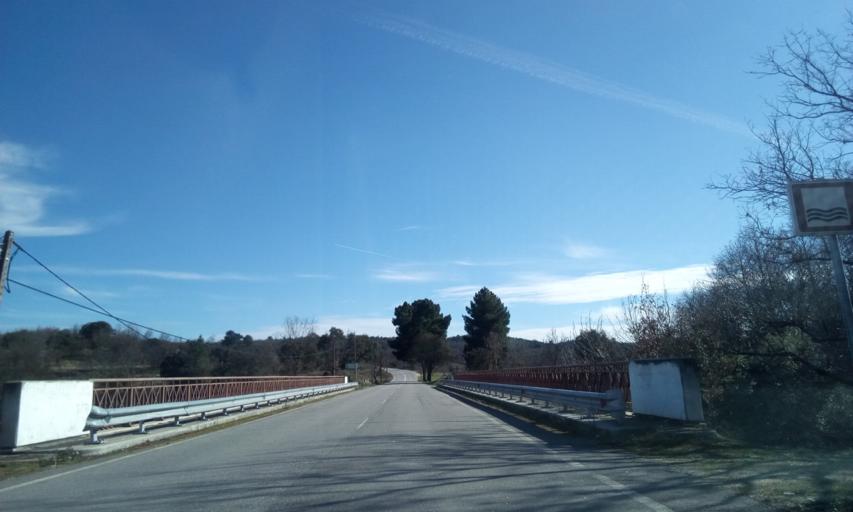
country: PT
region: Guarda
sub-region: Pinhel
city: Pinhel
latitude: 40.6025
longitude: -7.0325
